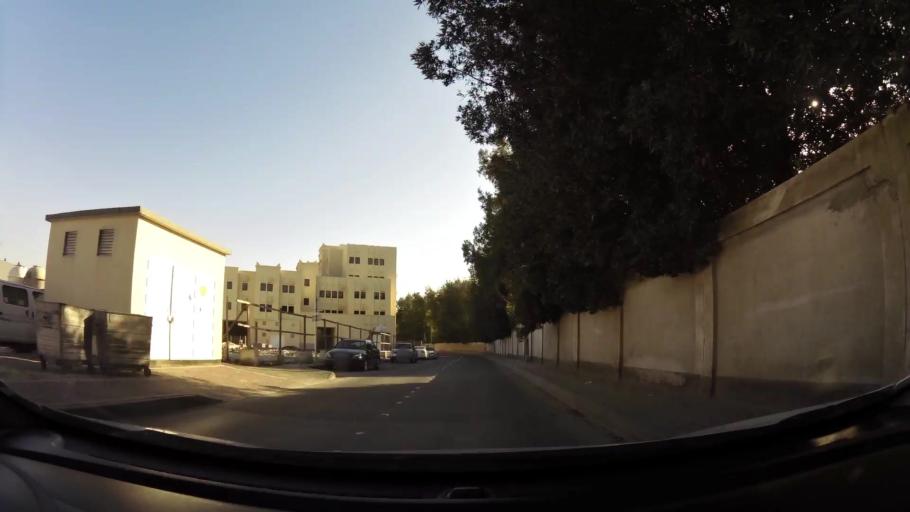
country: BH
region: Manama
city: Manama
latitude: 26.2306
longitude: 50.5856
